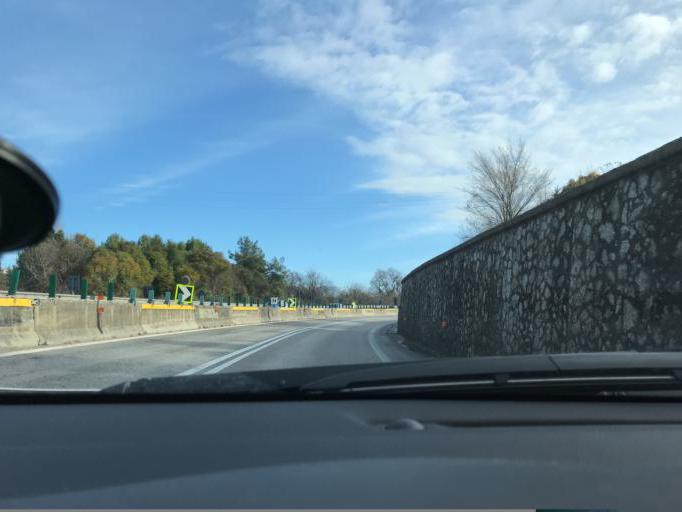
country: IT
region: The Marches
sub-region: Provincia di Ancona
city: Falconara Marittima
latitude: 43.6149
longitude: 13.3805
